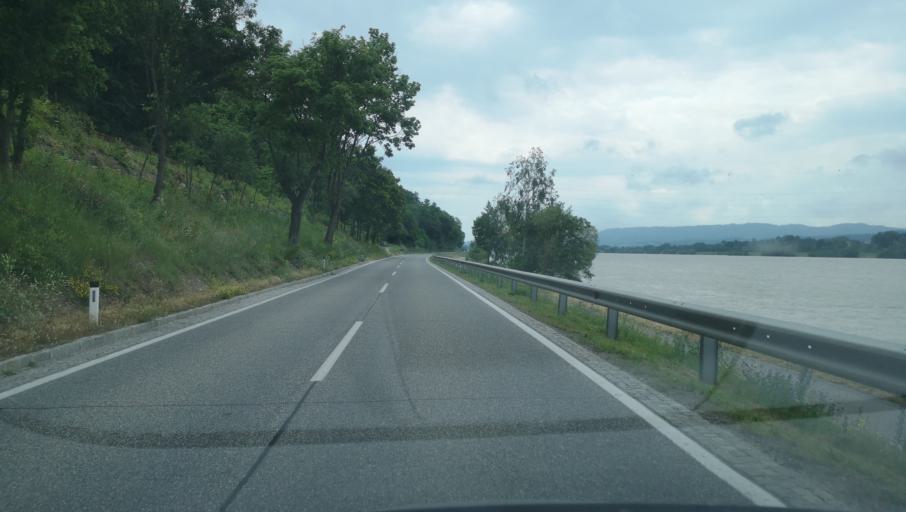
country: AT
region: Lower Austria
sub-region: Politischer Bezirk Melk
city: Pochlarn
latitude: 48.2177
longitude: 15.1818
